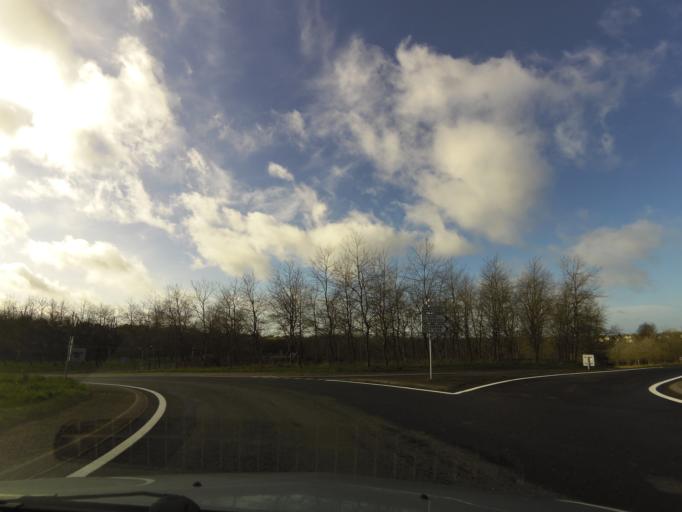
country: FR
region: Lower Normandy
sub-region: Departement du Calvados
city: Saint-Martin-des-Besaces
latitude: 49.0257
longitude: -0.8346
